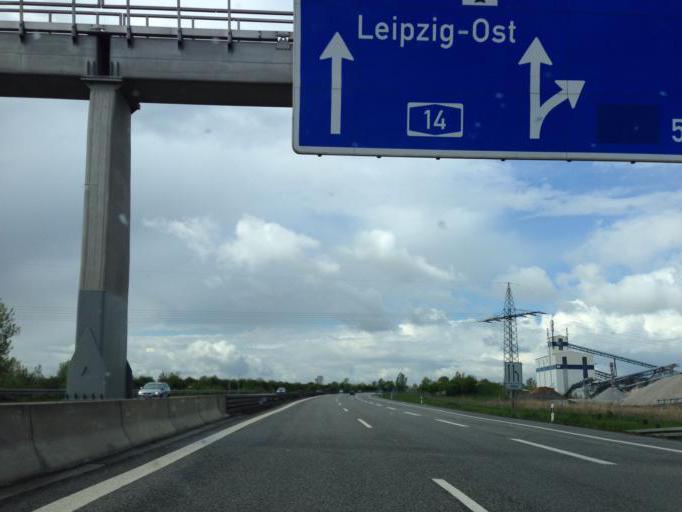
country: DE
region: Saxony
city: Borsdorf
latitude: 51.3148
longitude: 12.5315
